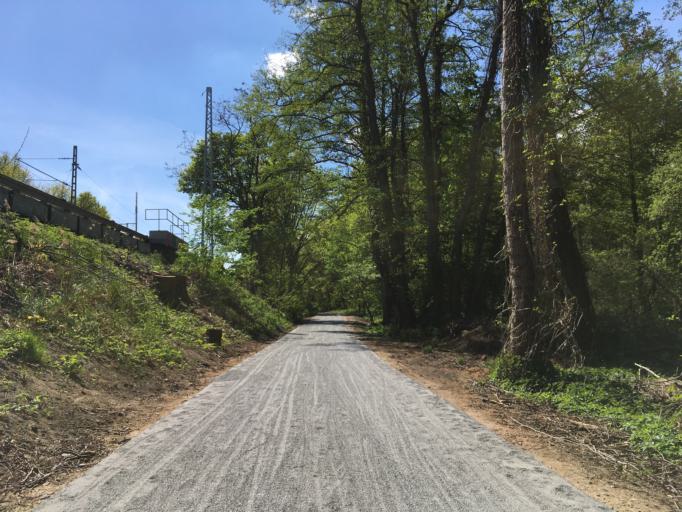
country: DE
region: Brandenburg
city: Bernau bei Berlin
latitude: 52.6630
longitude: 13.5417
